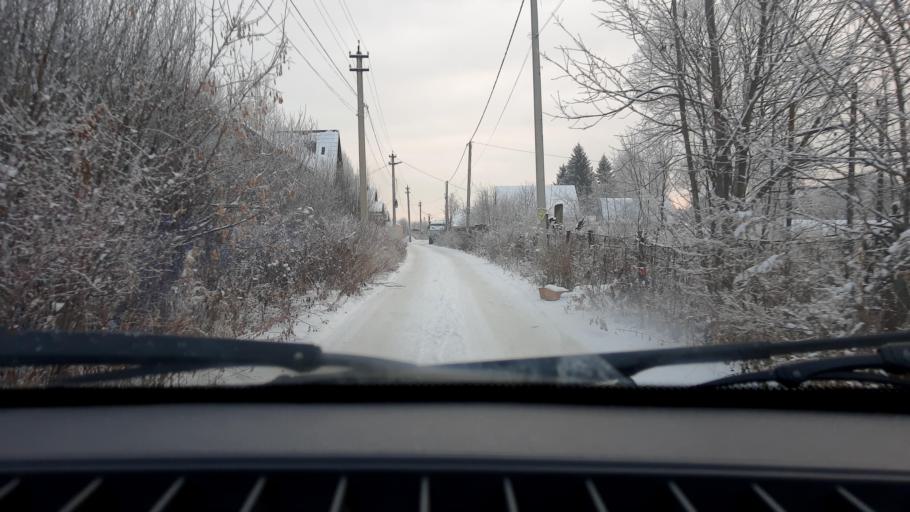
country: RU
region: Bashkortostan
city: Ufa
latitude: 54.6562
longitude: 55.9255
